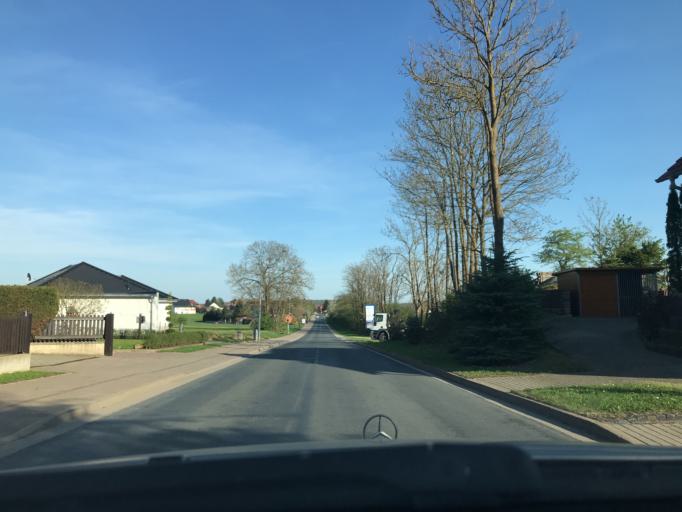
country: DE
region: Thuringia
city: Niederorschel
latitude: 51.3316
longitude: 10.4287
